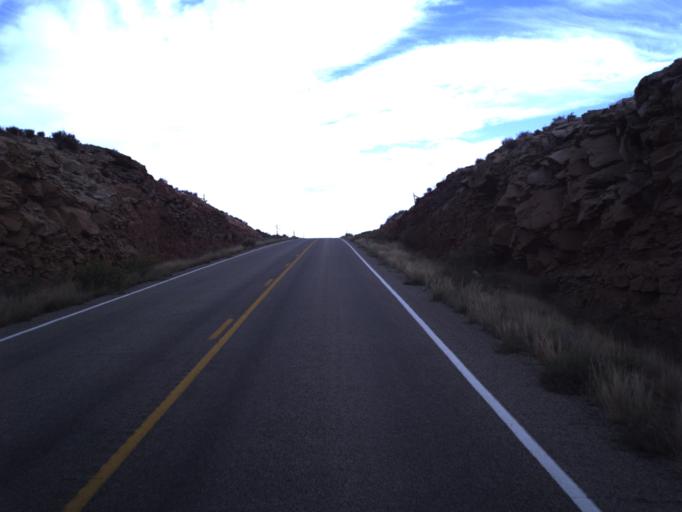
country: US
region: Utah
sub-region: San Juan County
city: Blanding
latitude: 37.2639
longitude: -109.6500
